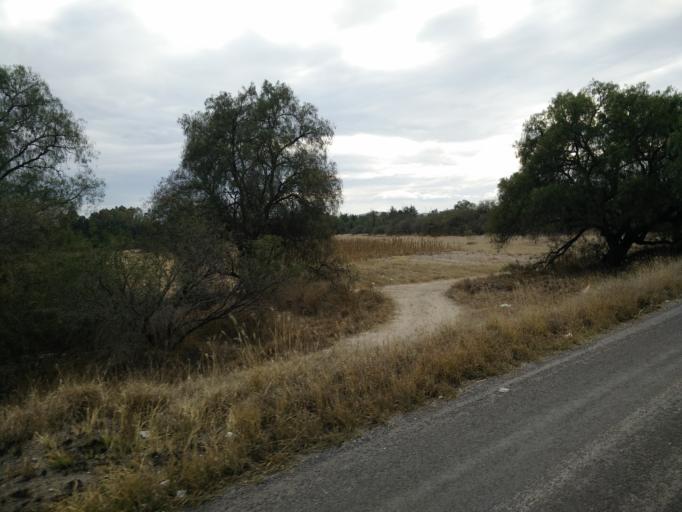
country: MX
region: Queretaro
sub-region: Tequisquiapan
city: Tequisquiapan
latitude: 20.5375
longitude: -99.8892
